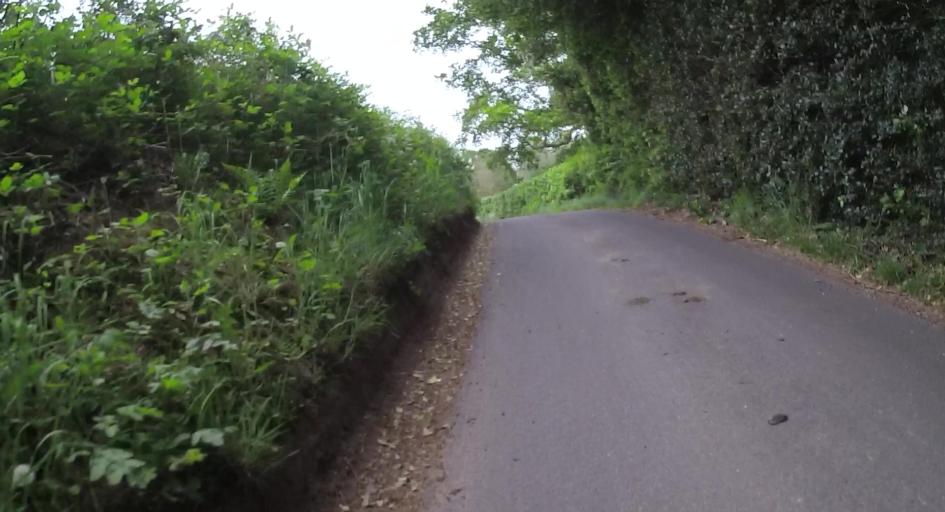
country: GB
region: England
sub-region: West Berkshire
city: Stratfield Mortimer
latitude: 51.3484
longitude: -1.0660
